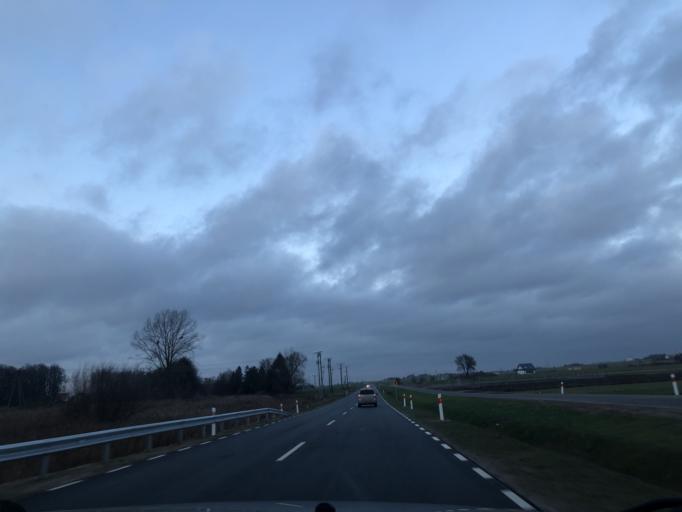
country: PL
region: Podlasie
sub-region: Lomza
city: Lomza
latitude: 53.1341
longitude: 22.0496
